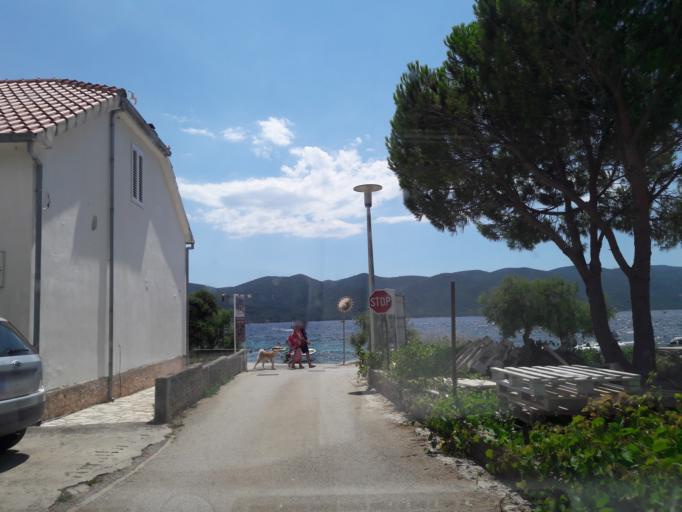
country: HR
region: Dubrovacko-Neretvanska
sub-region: Grad Korcula
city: Zrnovo
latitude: 42.9812
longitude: 17.1028
